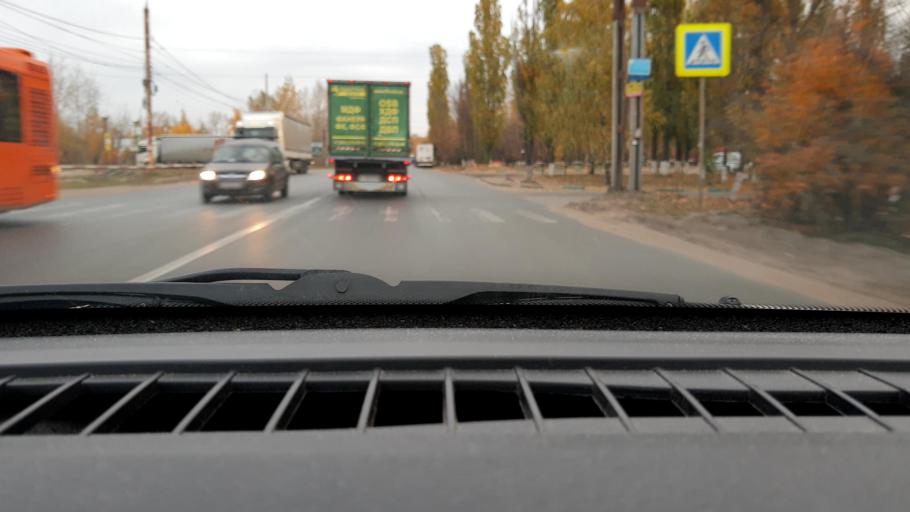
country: RU
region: Nizjnij Novgorod
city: Gorbatovka
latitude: 56.3543
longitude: 43.8038
